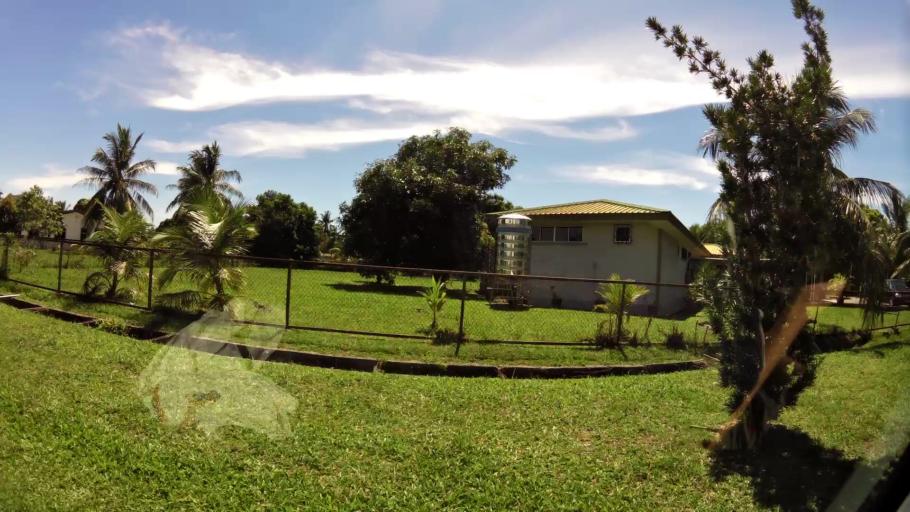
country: BN
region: Brunei and Muara
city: Bandar Seri Begawan
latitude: 5.0348
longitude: 115.0667
